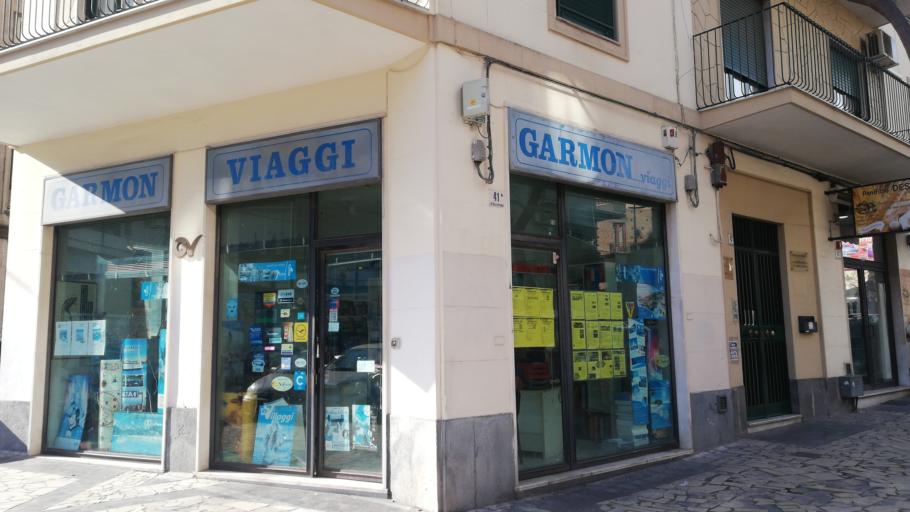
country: IT
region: Sicily
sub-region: Catania
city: Canalicchio
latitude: 37.5162
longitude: 15.0959
